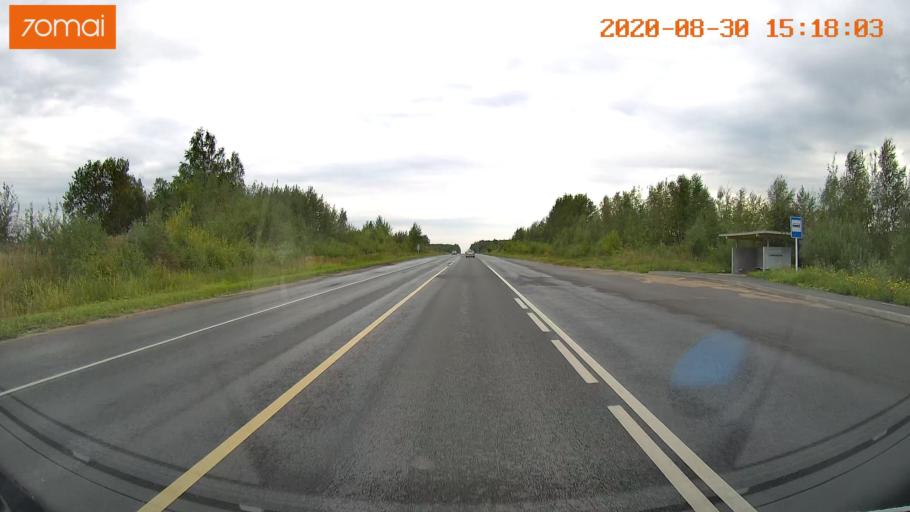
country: RU
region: Ivanovo
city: Rodniki
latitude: 57.1274
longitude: 41.7976
